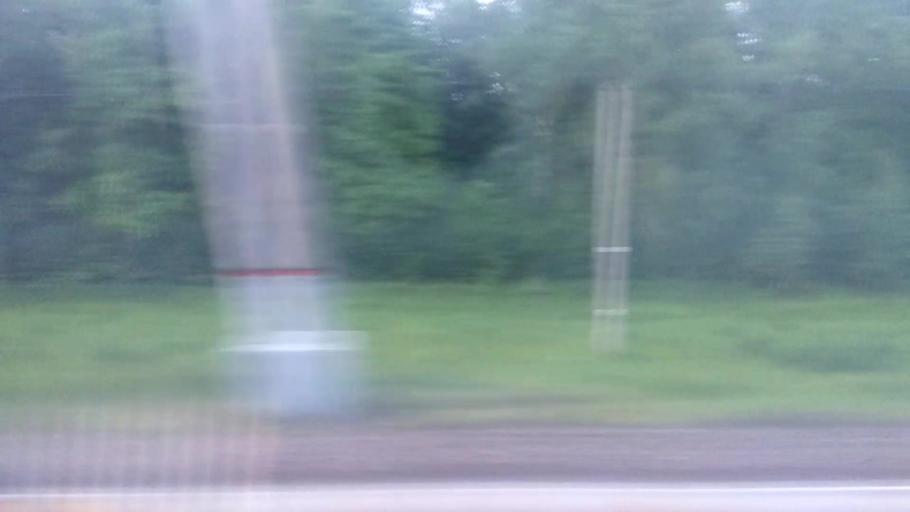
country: RU
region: Moskovskaya
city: Yam
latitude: 55.4828
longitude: 37.7374
